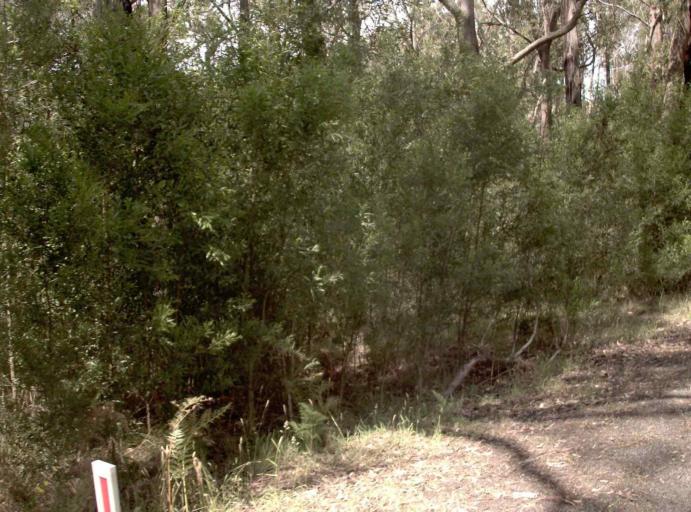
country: AU
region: Victoria
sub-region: Latrobe
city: Traralgon
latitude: -38.3067
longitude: 146.5526
